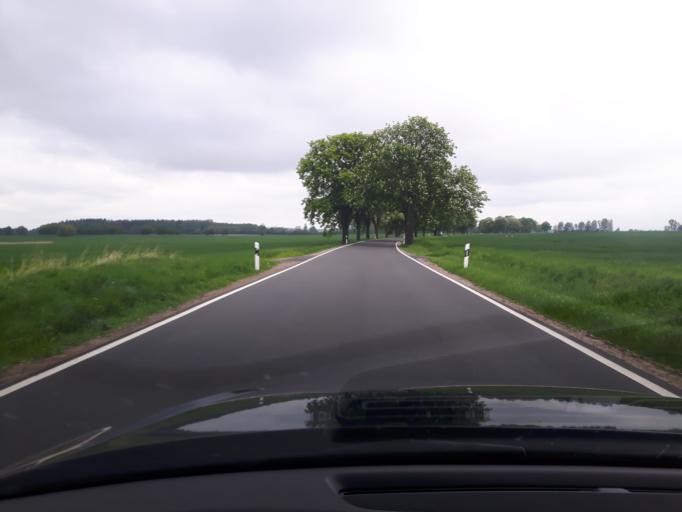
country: DE
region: Mecklenburg-Vorpommern
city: Bad Sulze
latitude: 54.0357
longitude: 12.6682
